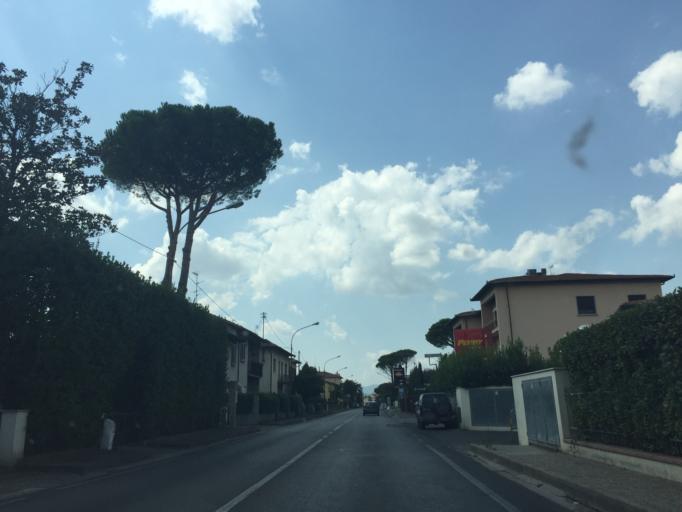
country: IT
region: Tuscany
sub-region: Province of Florence
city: San Mauro
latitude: 43.8049
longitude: 11.1233
